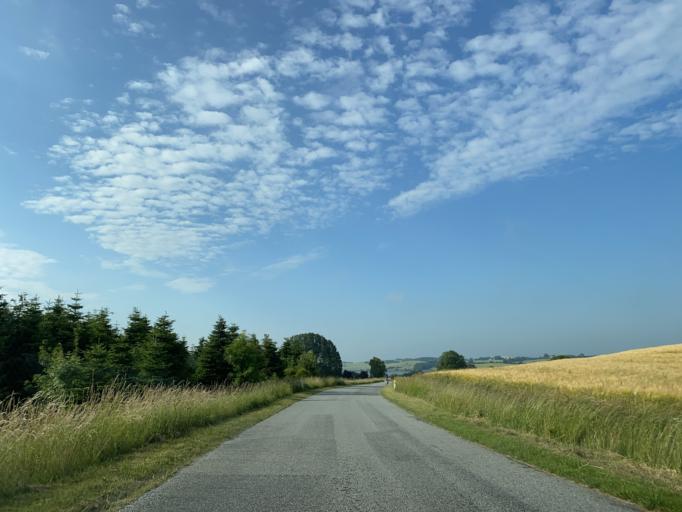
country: DK
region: South Denmark
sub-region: Haderslev Kommune
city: Haderslev
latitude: 55.1800
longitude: 9.4817
